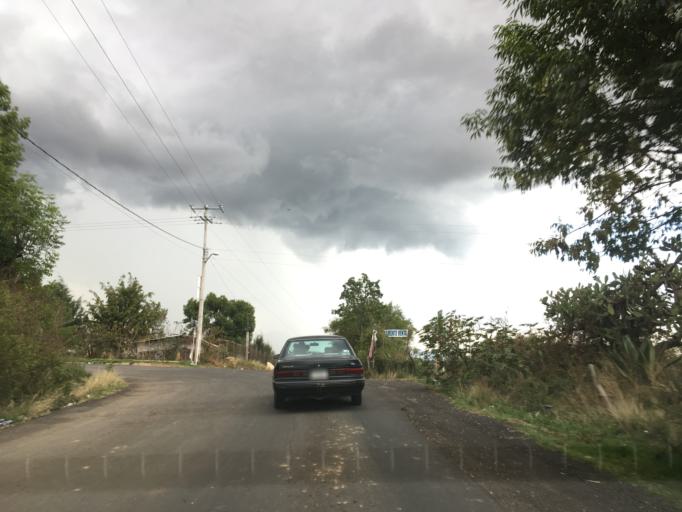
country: MX
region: Michoacan
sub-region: Morelia
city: La Mintzita (Piedra Dura)
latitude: 19.5941
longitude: -101.2737
